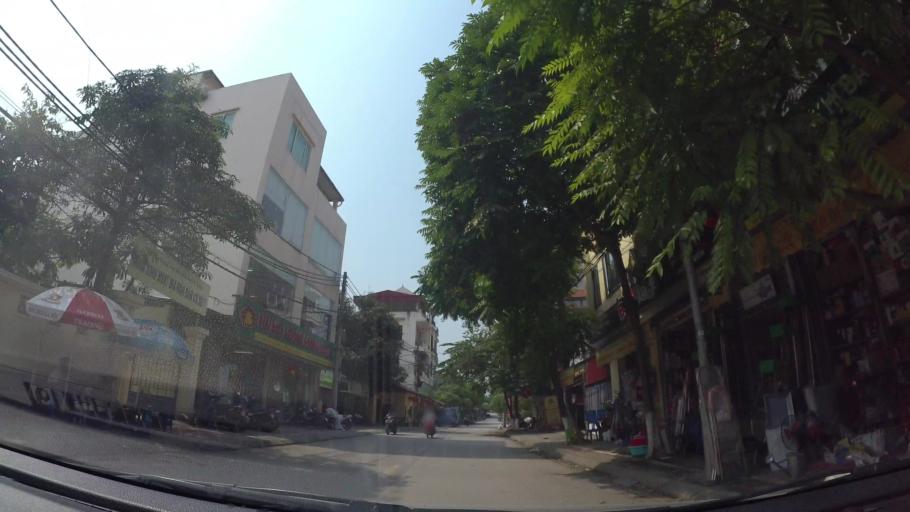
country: VN
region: Ha Noi
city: Tay Ho
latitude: 21.0878
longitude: 105.8091
